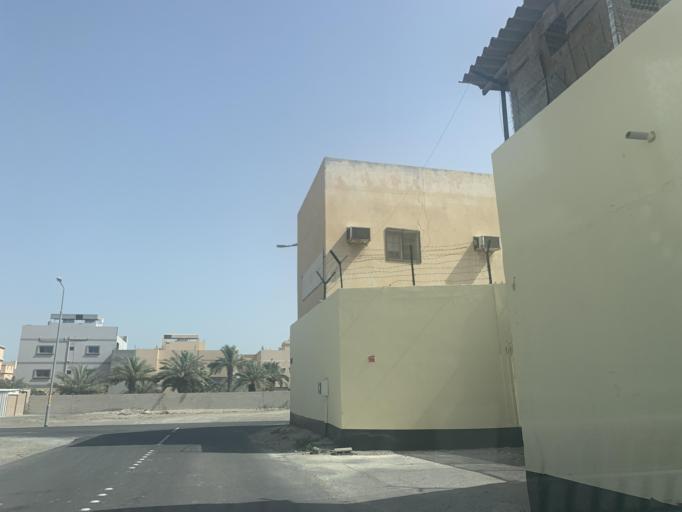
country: BH
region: Northern
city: Sitrah
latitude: 26.1643
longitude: 50.6188
